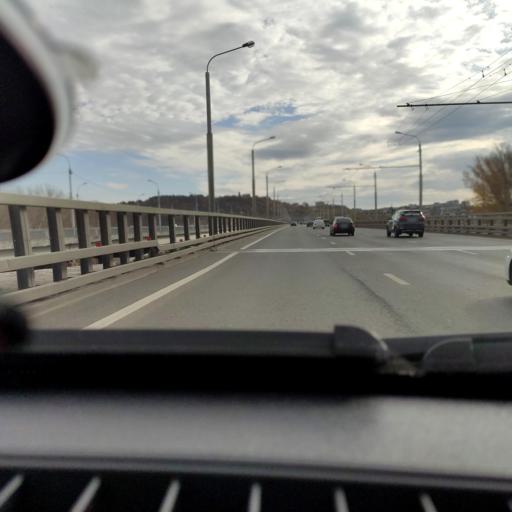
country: RU
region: Bashkortostan
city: Ufa
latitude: 54.7585
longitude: 55.9599
